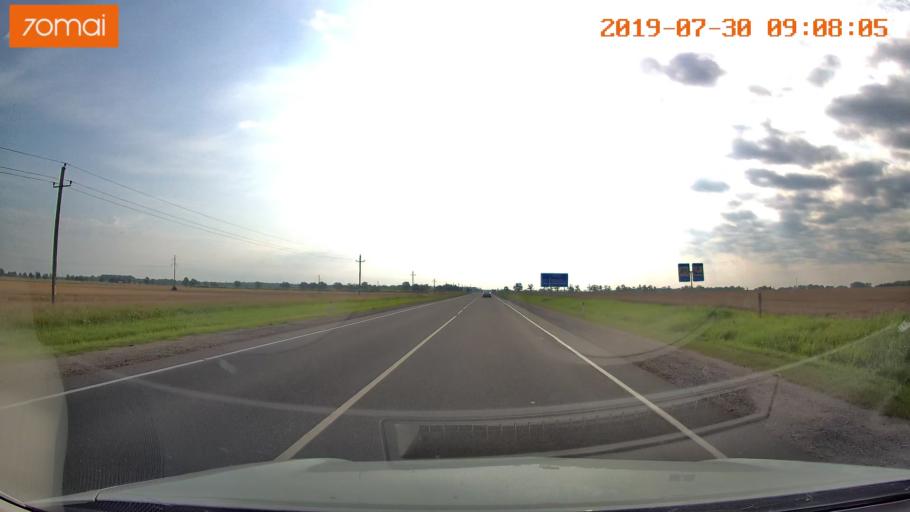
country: RU
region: Kaliningrad
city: Gusev
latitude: 54.6124
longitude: 22.3776
